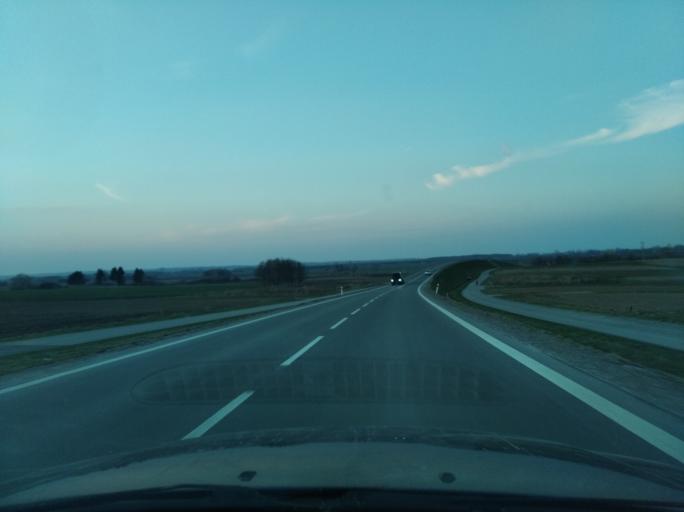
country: PL
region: Subcarpathian Voivodeship
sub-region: Powiat przeworski
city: Grzeska
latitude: 50.0726
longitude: 22.4712
